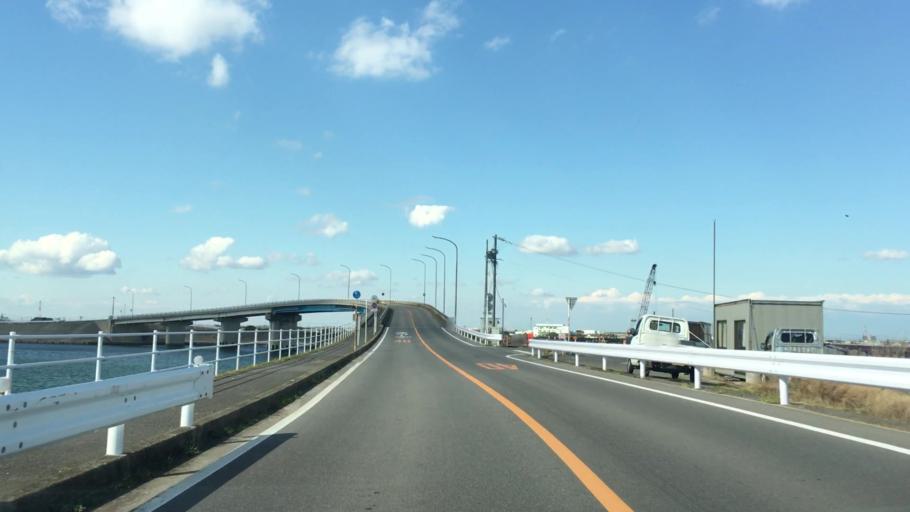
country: JP
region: Aichi
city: Ishiki
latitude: 34.7926
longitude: 137.0182
